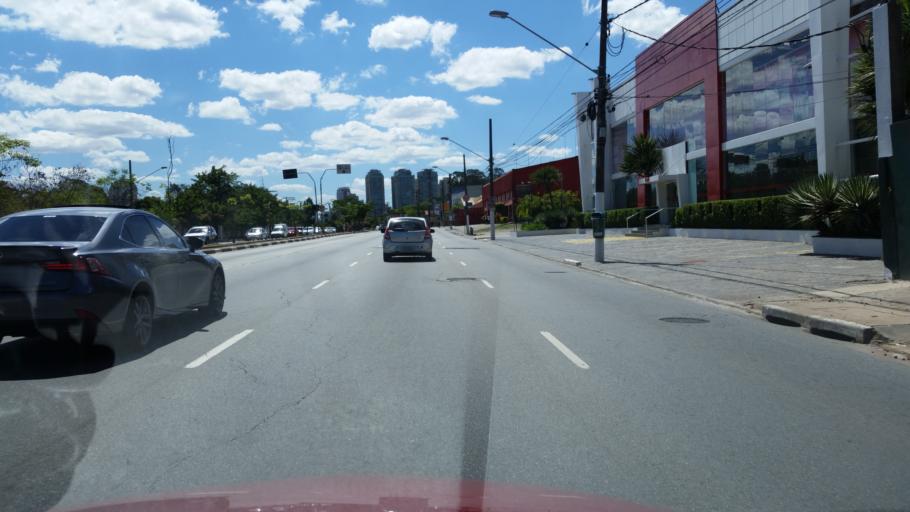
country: BR
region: Sao Paulo
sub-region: Diadema
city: Diadema
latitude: -23.6358
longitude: -46.6780
